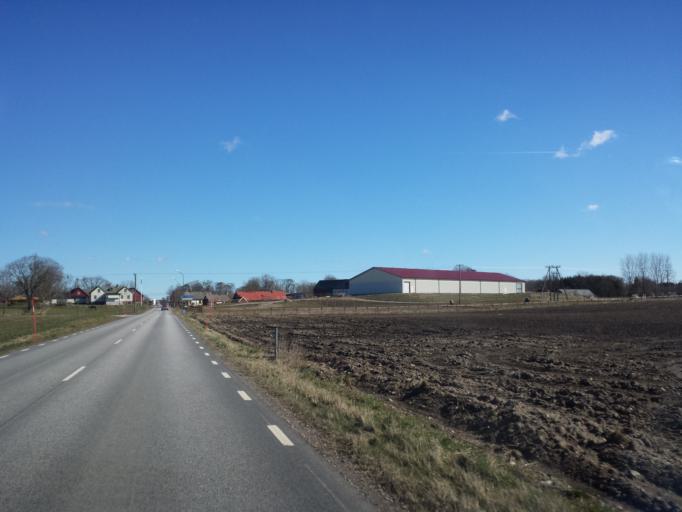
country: SE
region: Skane
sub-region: Tomelilla Kommun
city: Tomelilla
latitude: 55.6433
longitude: 13.8866
